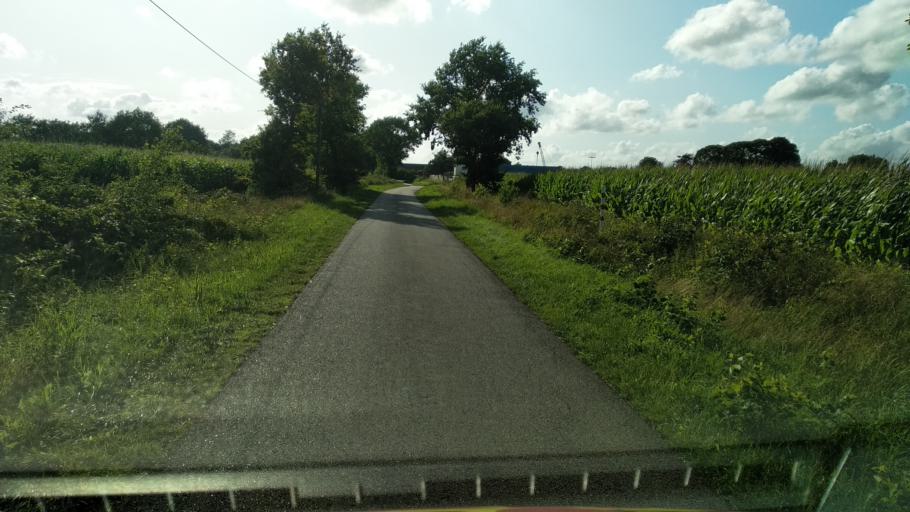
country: DE
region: Schleswig-Holstein
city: Gross Rheide
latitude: 54.4293
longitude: 9.4178
